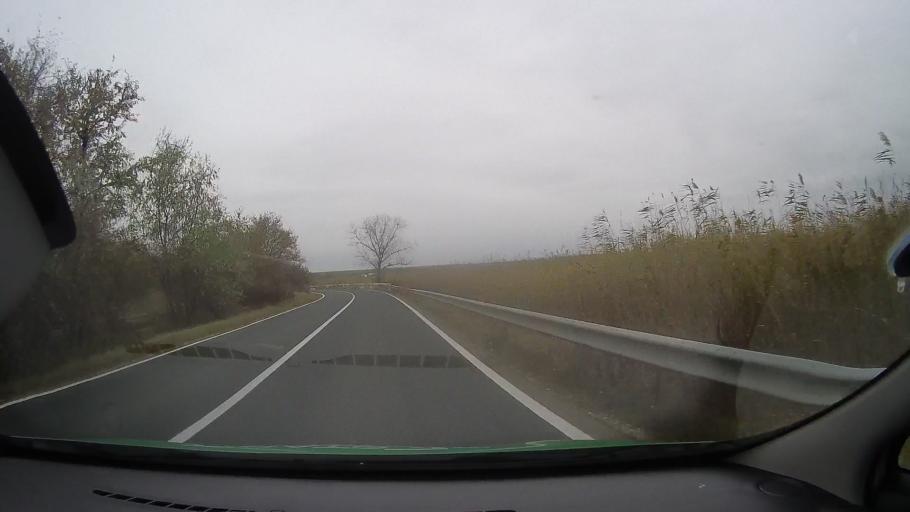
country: RO
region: Constanta
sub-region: Comuna Garliciu
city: Garliciu
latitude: 44.7077
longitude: 28.0641
